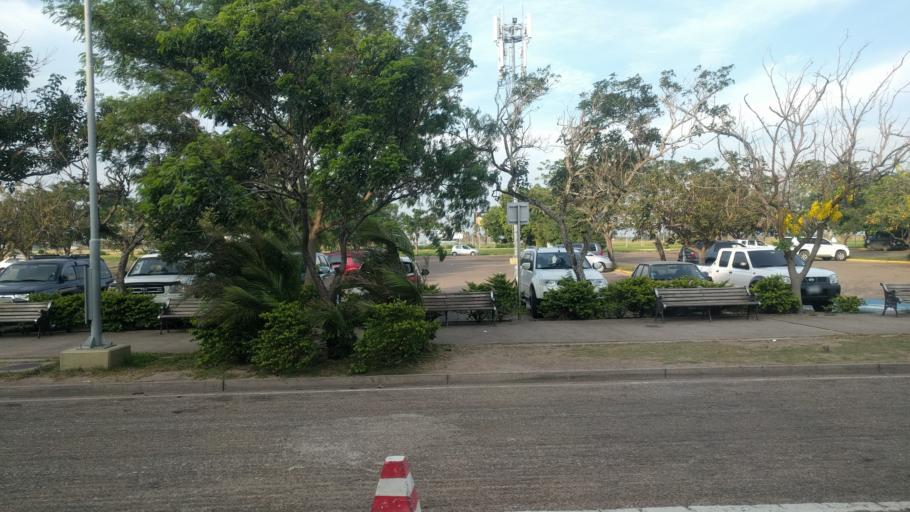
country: BO
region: Santa Cruz
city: La Belgica
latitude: -17.6477
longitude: -63.1407
